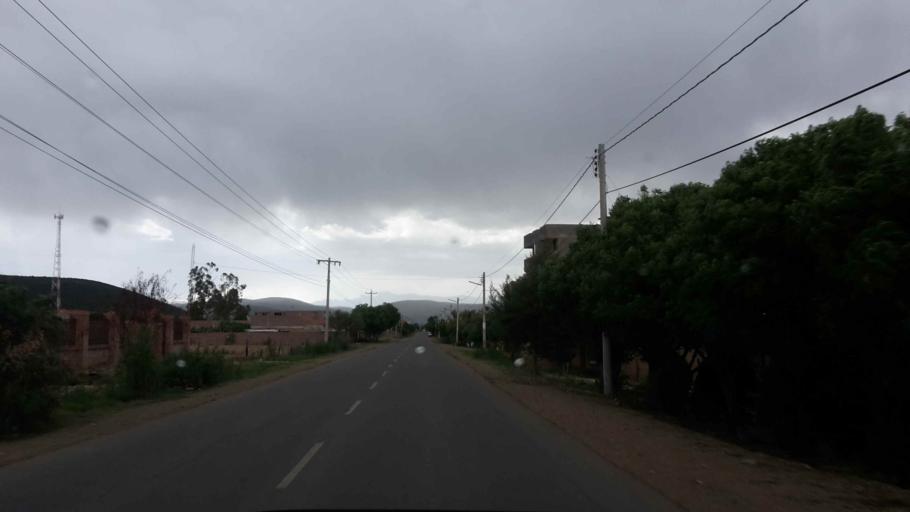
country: BO
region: Cochabamba
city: Tarata
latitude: -17.5878
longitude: -66.0490
